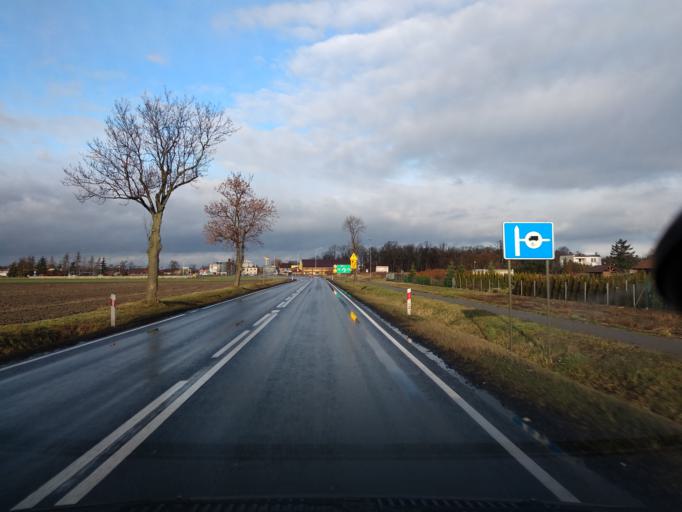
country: PL
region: Greater Poland Voivodeship
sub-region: Powiat koninski
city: Rychwal
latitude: 52.0642
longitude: 18.1639
